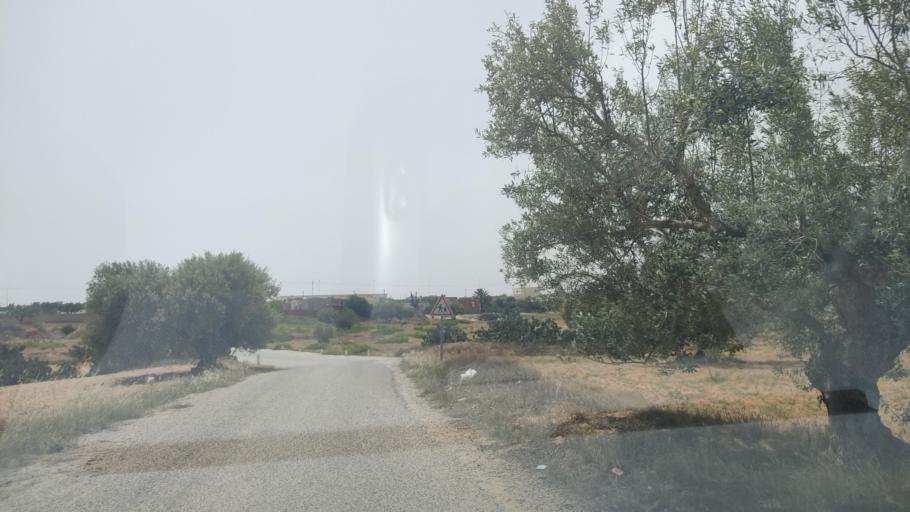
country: TN
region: Safaqis
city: Sfax
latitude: 34.8327
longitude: 10.6003
